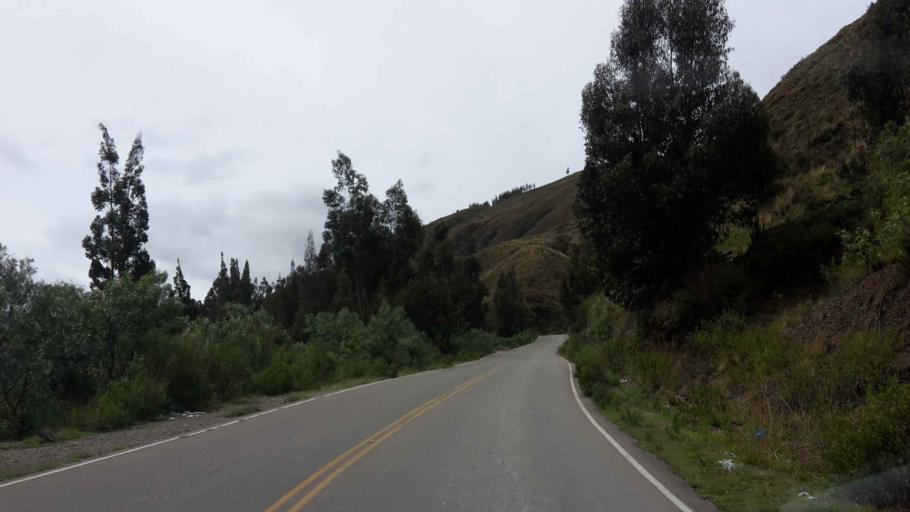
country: BO
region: Cochabamba
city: Colomi
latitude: -17.4067
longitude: -65.7885
